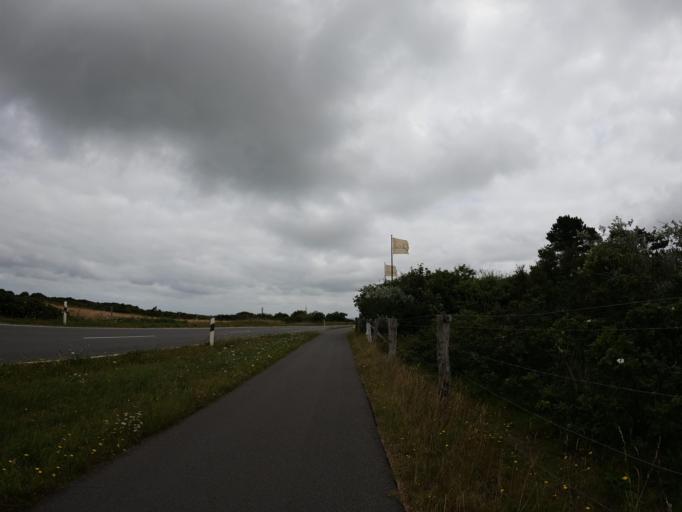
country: DE
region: Schleswig-Holstein
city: Tinnum
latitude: 54.9269
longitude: 8.3549
